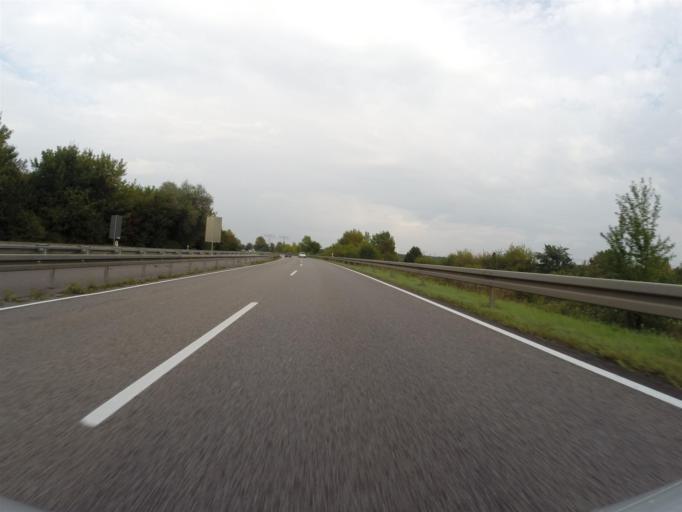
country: DE
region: Saxony-Anhalt
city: Halle Neustadt
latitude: 51.4649
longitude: 11.9241
